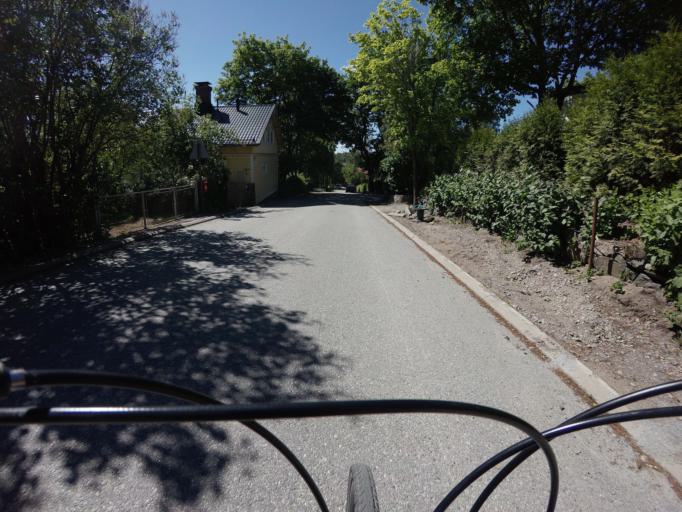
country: FI
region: Varsinais-Suomi
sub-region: Turku
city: Raisio
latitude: 60.4512
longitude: 22.2100
